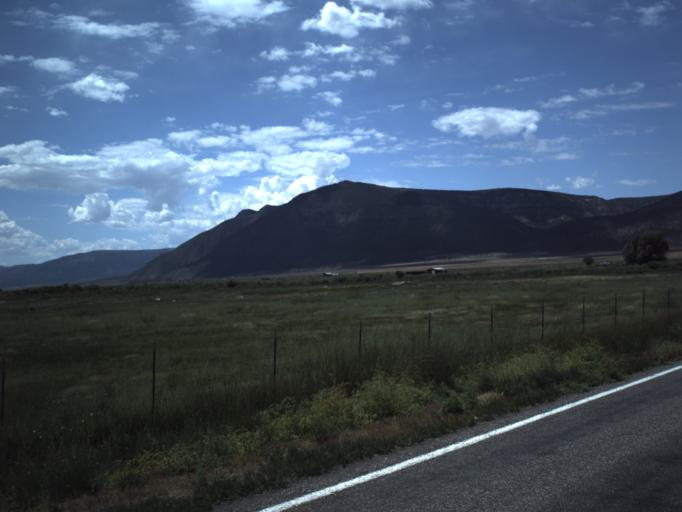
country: US
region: Utah
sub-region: Sanpete County
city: Moroni
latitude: 39.4758
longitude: -111.5938
